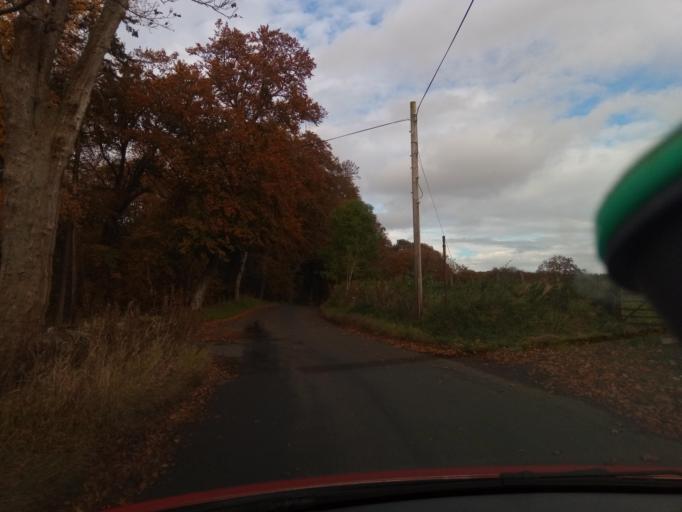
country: GB
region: Scotland
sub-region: South Lanarkshire
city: Carnwath
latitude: 55.7358
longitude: -3.6042
